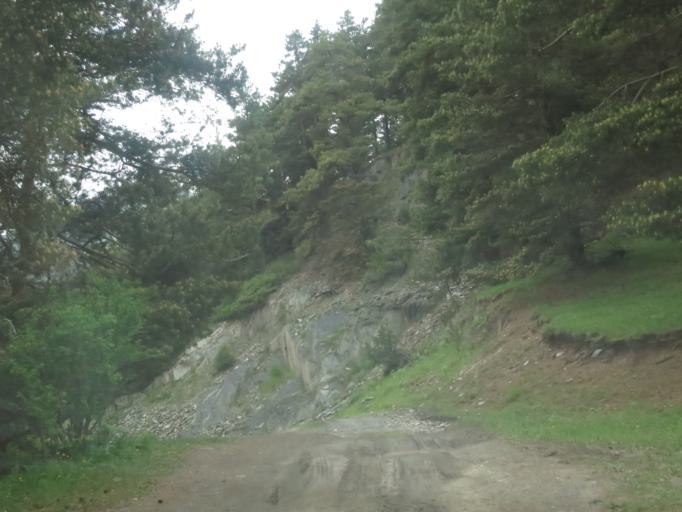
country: RU
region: Chechnya
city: Itum-Kali
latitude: 42.3674
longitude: 45.6530
